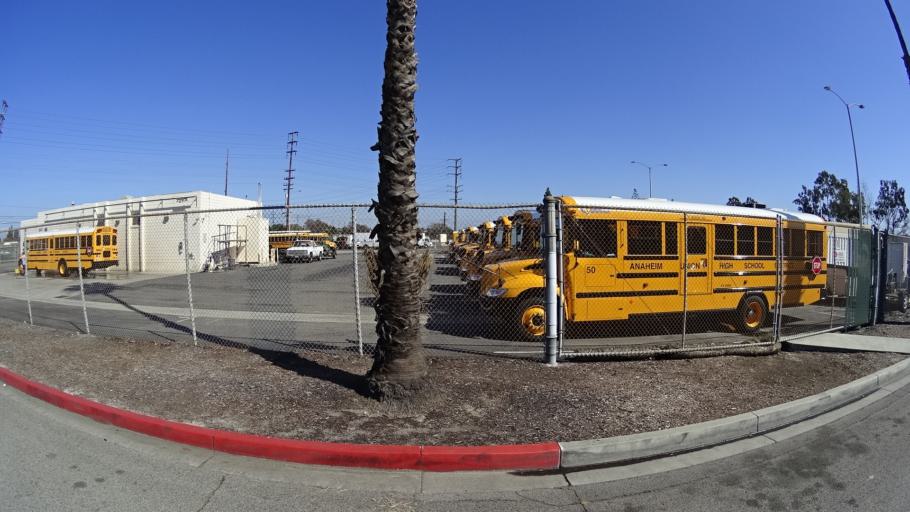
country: US
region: California
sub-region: Orange County
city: Anaheim
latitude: 33.8388
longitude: -117.9502
